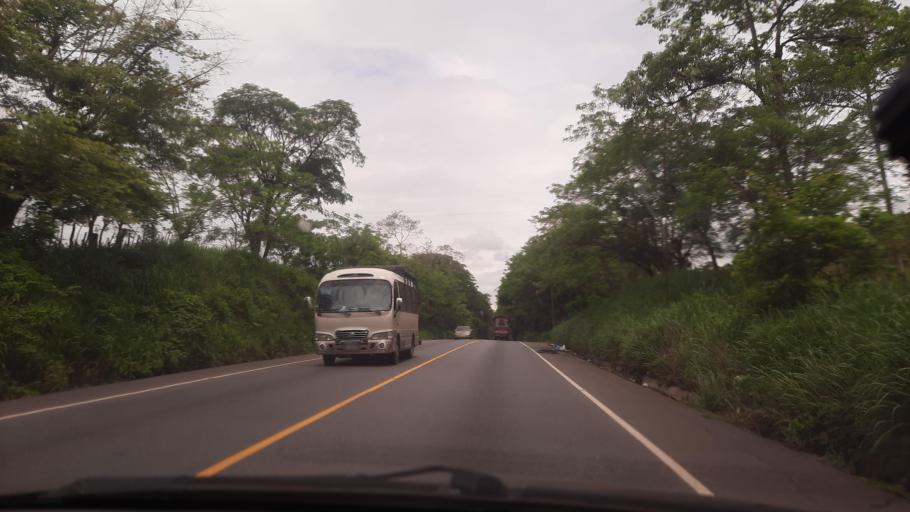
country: GT
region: Izabal
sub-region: Municipio de Los Amates
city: Los Amates
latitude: 15.2204
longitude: -89.2213
